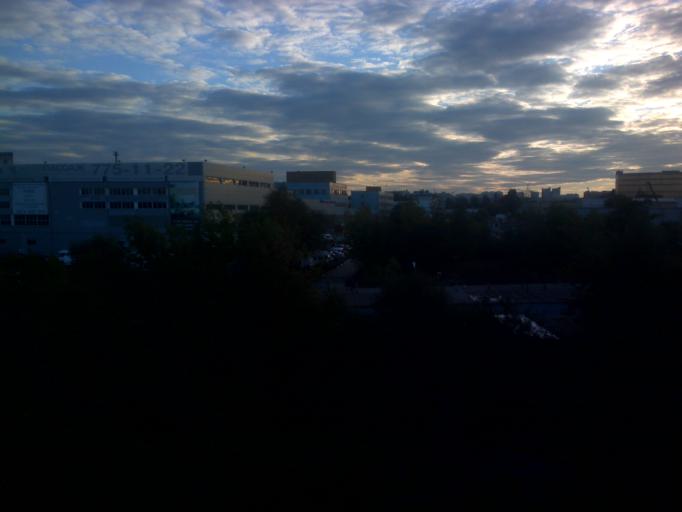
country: RU
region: Moscow
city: Tsaritsyno
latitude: 55.6137
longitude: 37.6356
